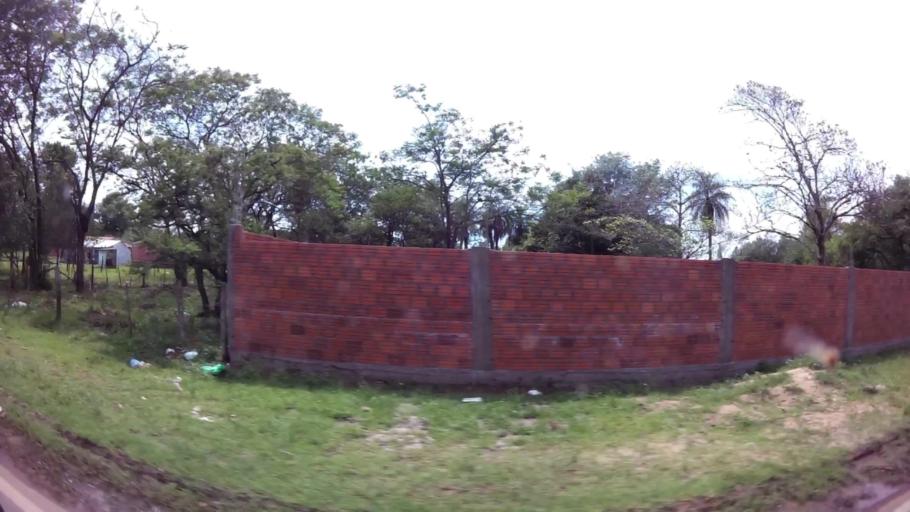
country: PY
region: Central
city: Limpio
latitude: -25.1804
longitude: -57.4738
